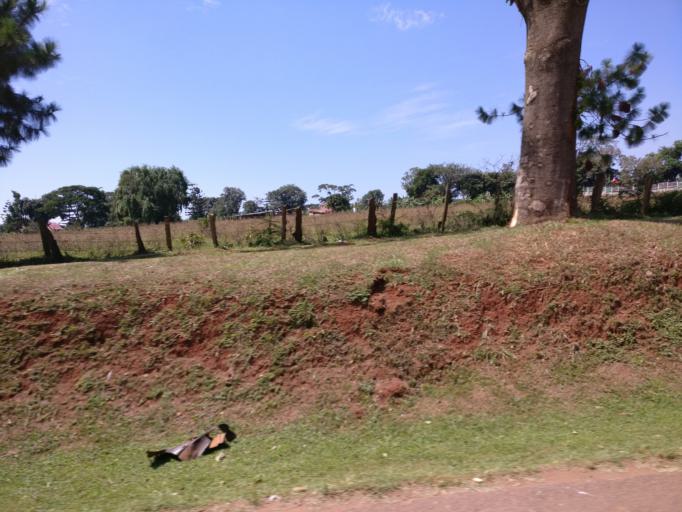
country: UG
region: Central Region
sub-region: Wakiso District
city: Kajansi
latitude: 0.1253
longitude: 32.5304
